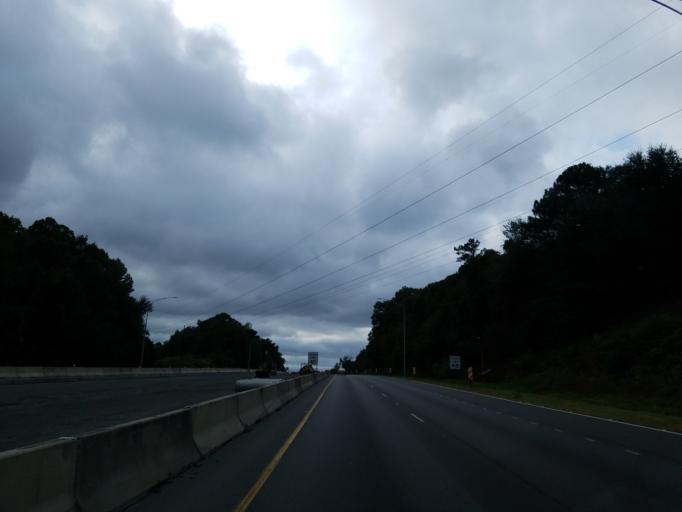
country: US
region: Alabama
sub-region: Tuscaloosa County
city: Holt
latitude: 33.1750
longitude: -87.4792
